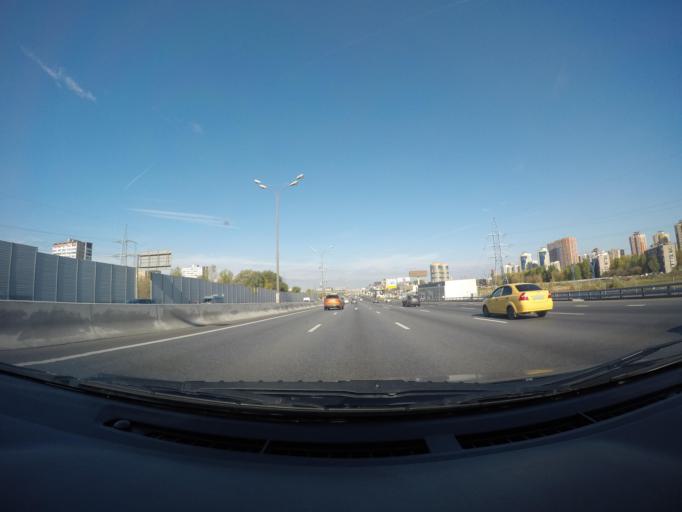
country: RU
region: Moscow
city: Ivanovskoye
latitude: 55.7512
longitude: 37.8423
